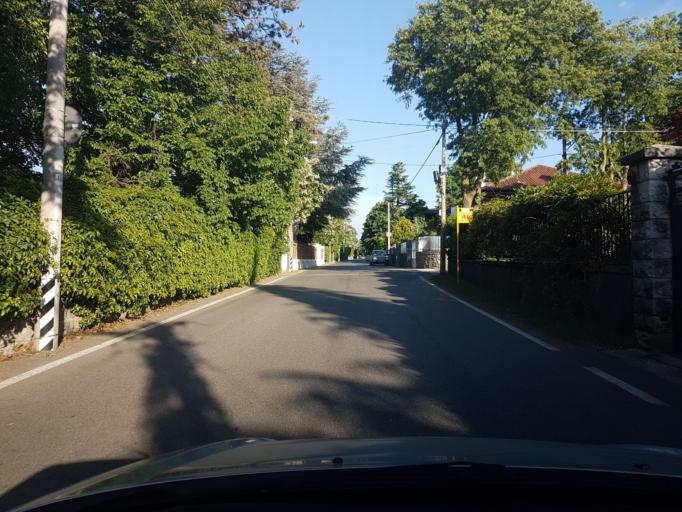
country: IT
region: Friuli Venezia Giulia
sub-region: Provincia di Trieste
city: Villa Opicina
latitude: 45.6878
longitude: 13.7800
